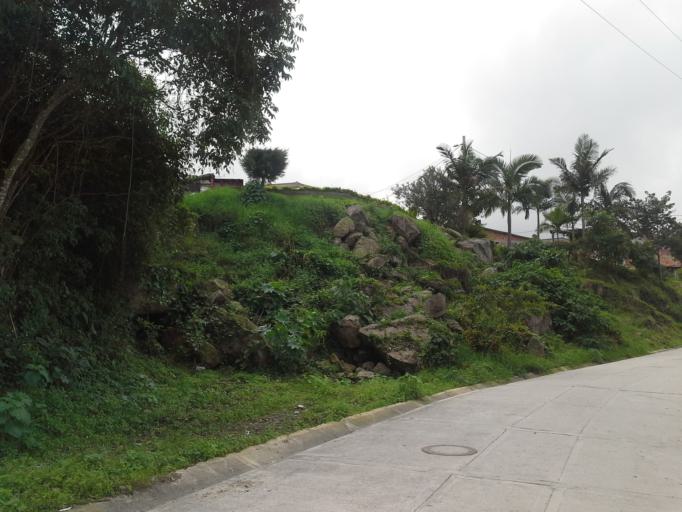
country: CO
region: Cundinamarca
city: San Antonio del Tequendama
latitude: 4.5913
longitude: -74.3395
